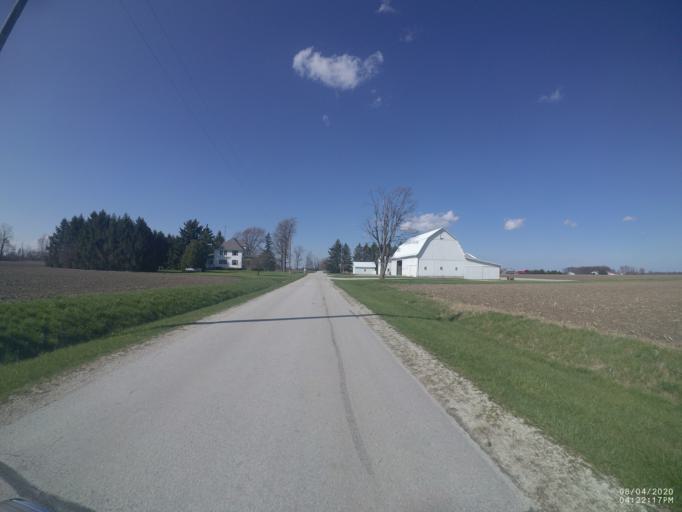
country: US
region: Ohio
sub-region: Sandusky County
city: Stony Prairie
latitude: 41.2862
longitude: -83.2165
